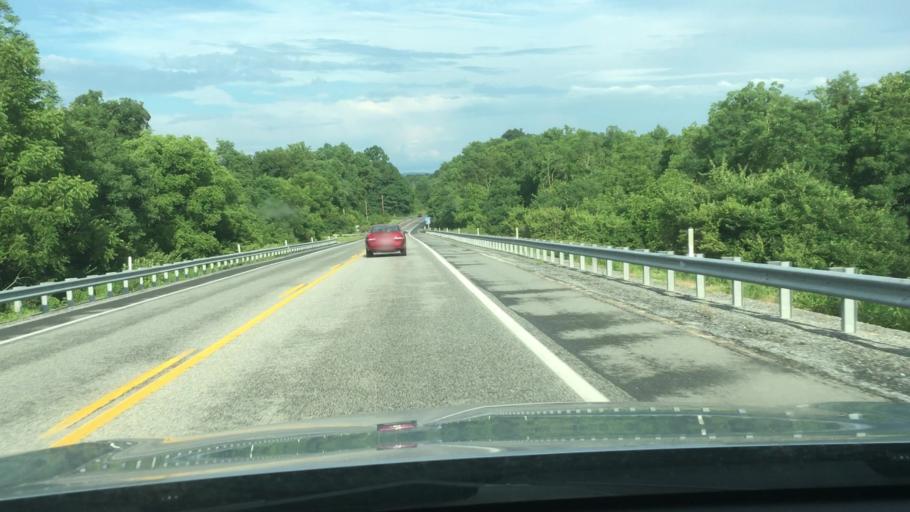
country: US
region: Pennsylvania
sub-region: York County
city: Dillsburg
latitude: 40.0955
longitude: -76.9640
